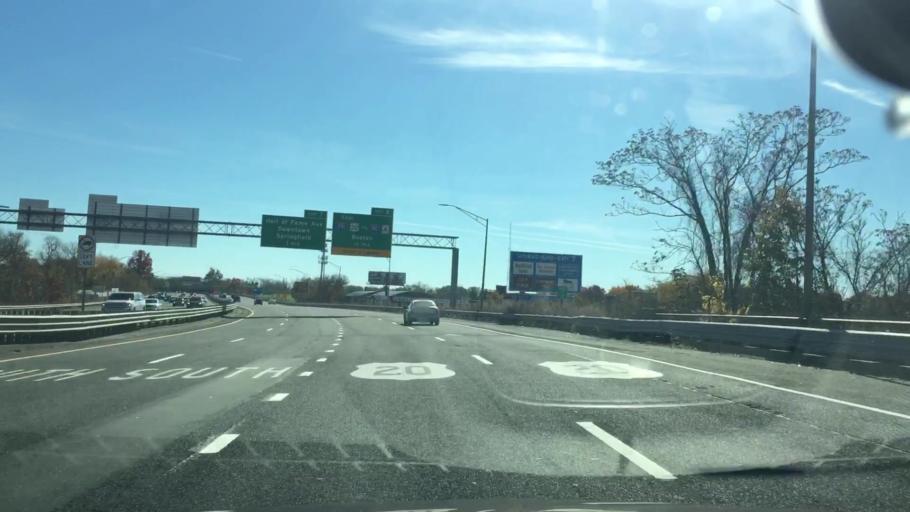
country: US
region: Massachusetts
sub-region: Hampden County
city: West Springfield
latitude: 42.1189
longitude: -72.6098
